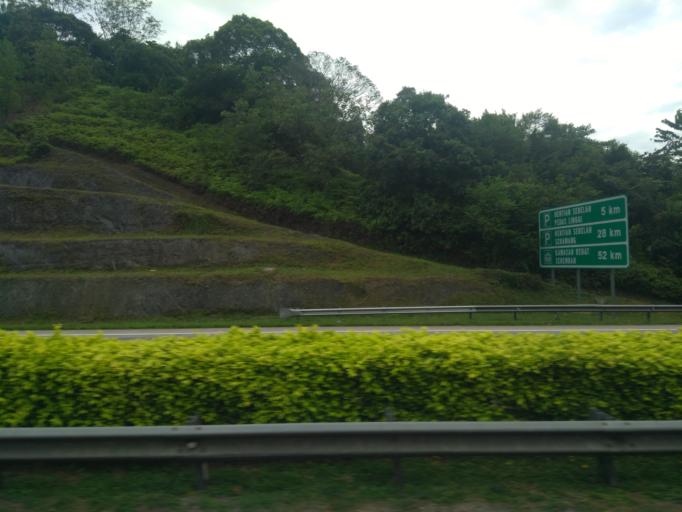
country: MY
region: Negeri Sembilan
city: Tampin
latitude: 2.4547
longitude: 102.1665
